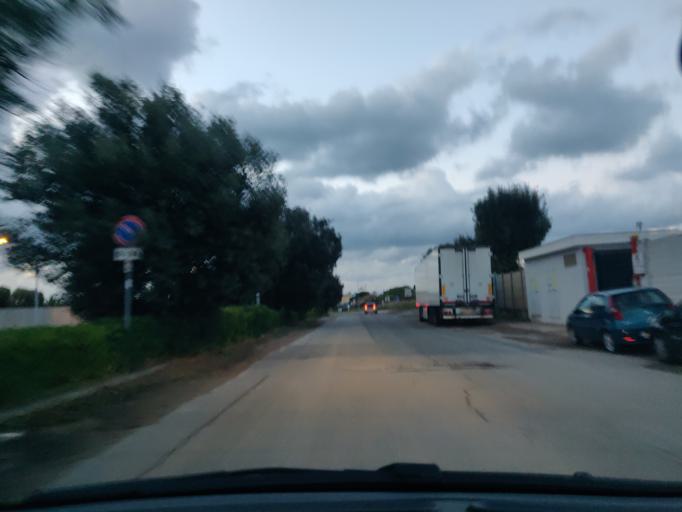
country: IT
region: Latium
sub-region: Citta metropolitana di Roma Capitale
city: Aurelia
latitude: 42.1173
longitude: 11.7787
